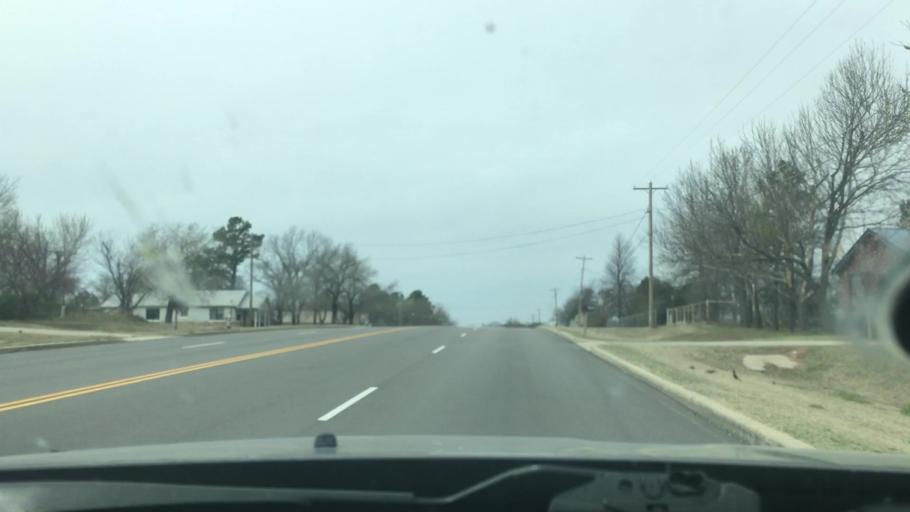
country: US
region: Oklahoma
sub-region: Seminole County
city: Seminole
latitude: 35.2557
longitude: -96.7082
